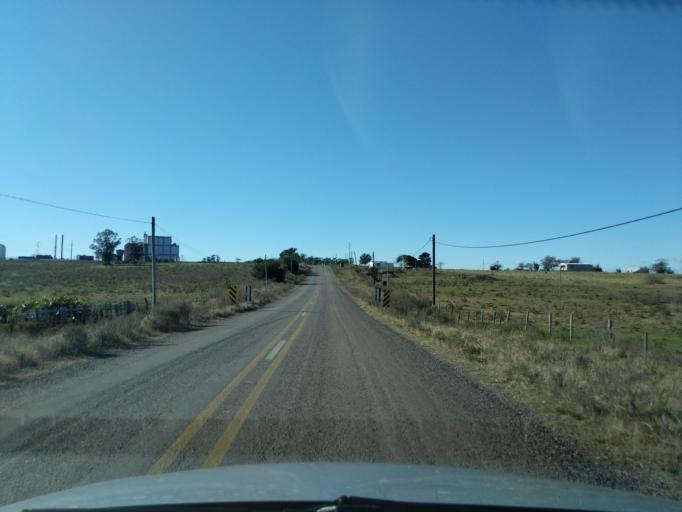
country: UY
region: Florida
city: Florida
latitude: -34.0522
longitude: -56.2449
